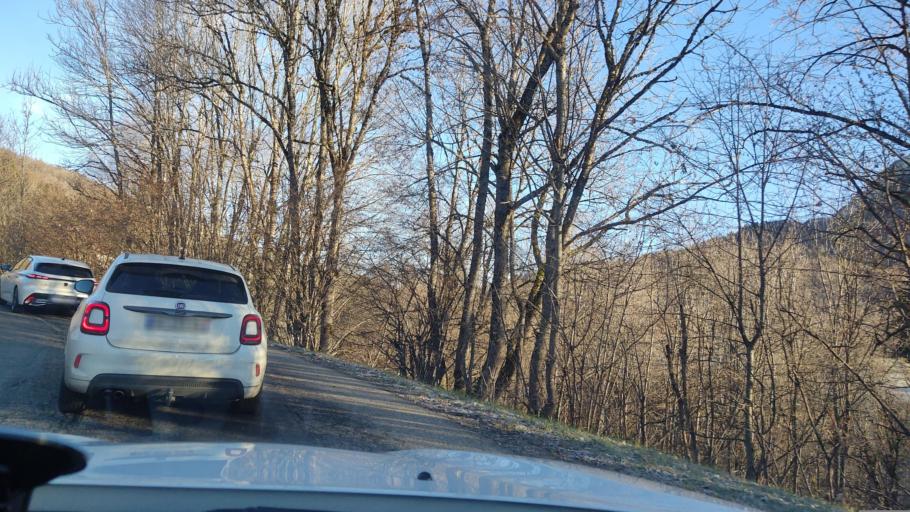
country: FR
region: Rhone-Alpes
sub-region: Departement de la Savoie
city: Barby
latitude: 45.6287
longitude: 6.0071
